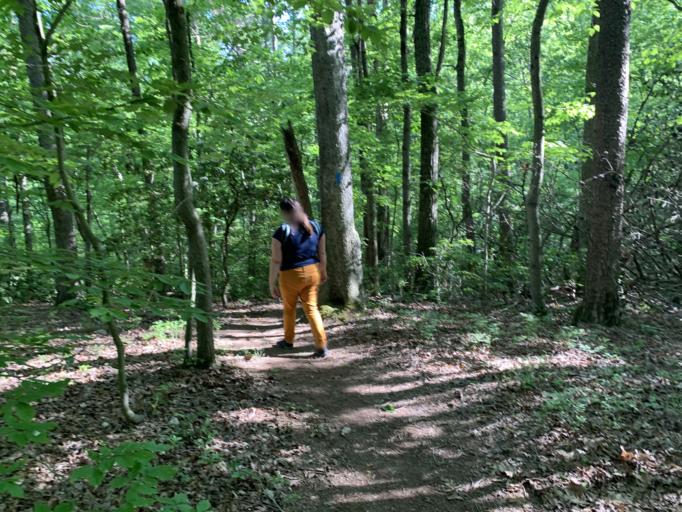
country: US
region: Maryland
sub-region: Cecil County
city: North East
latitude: 39.5751
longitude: -75.8876
